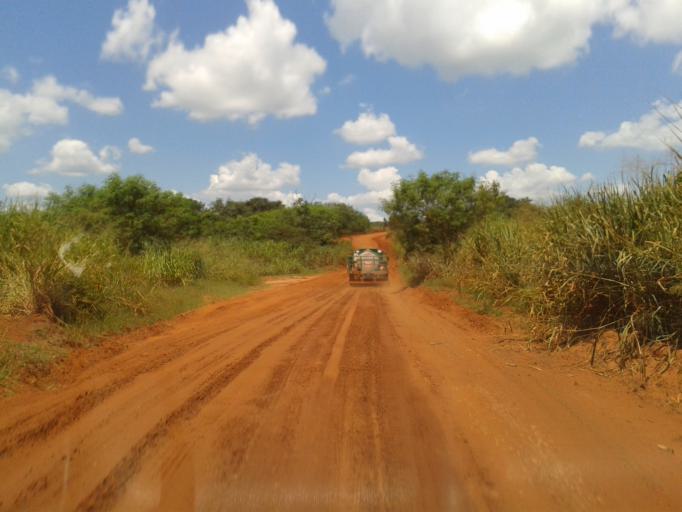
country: BR
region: Minas Gerais
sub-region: Ituiutaba
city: Ituiutaba
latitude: -18.9824
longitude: -49.6647
